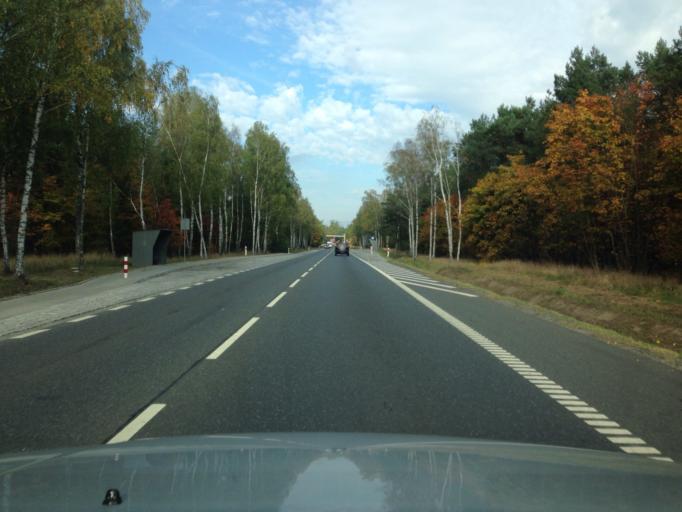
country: PL
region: Kujawsko-Pomorskie
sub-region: Grudziadz
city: Grudziadz
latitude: 53.5155
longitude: 18.6882
